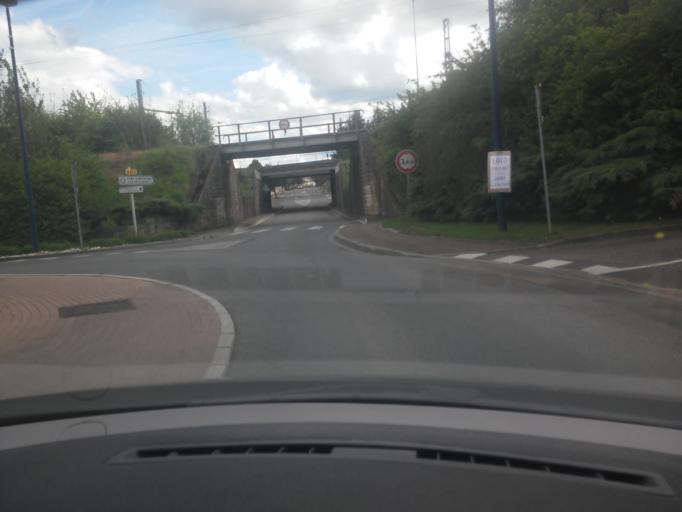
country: FR
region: Lorraine
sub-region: Departement de Meurthe-et-Moselle
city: Labry
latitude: 49.1664
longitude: 5.8819
